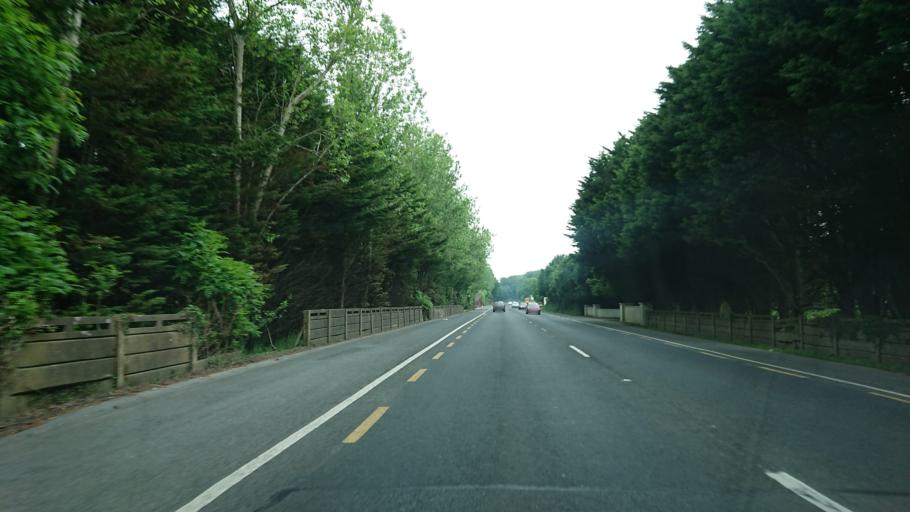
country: IE
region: Munster
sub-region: Waterford
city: Waterford
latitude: 52.2048
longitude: -7.1162
